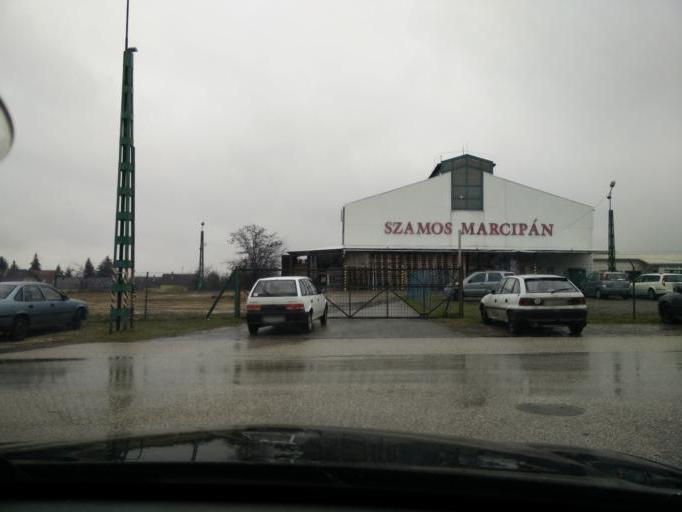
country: HU
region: Pest
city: Pilisszentivan
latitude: 47.6123
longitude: 18.9005
